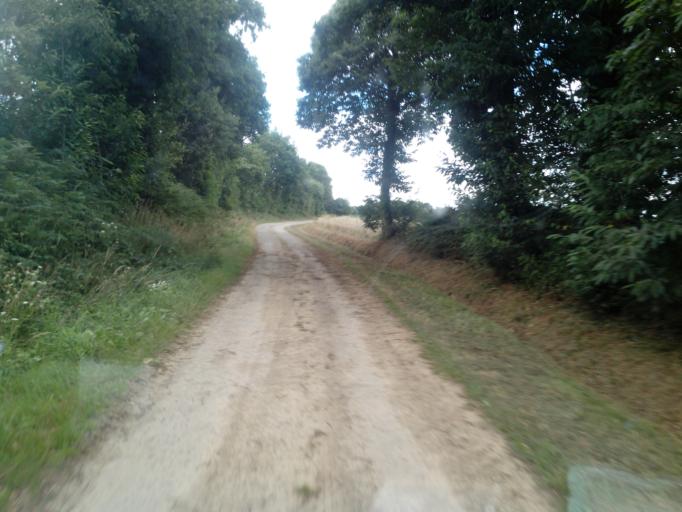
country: FR
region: Brittany
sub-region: Departement du Morbihan
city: Meneac
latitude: 48.1162
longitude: -2.4158
